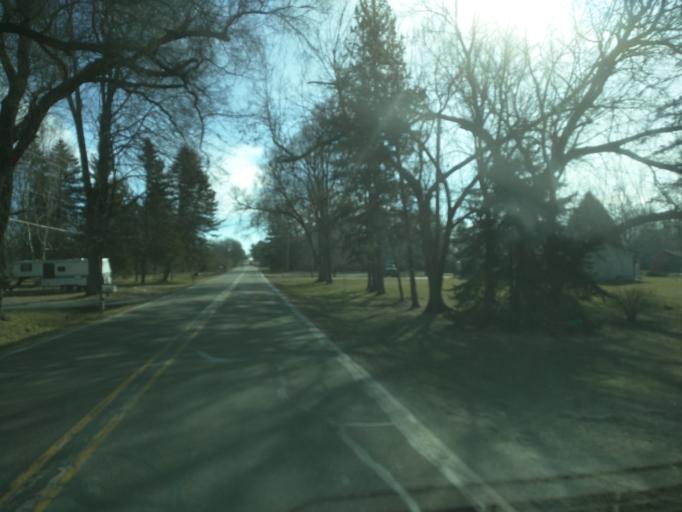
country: US
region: Michigan
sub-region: Ingham County
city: Haslett
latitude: 42.7751
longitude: -84.4253
